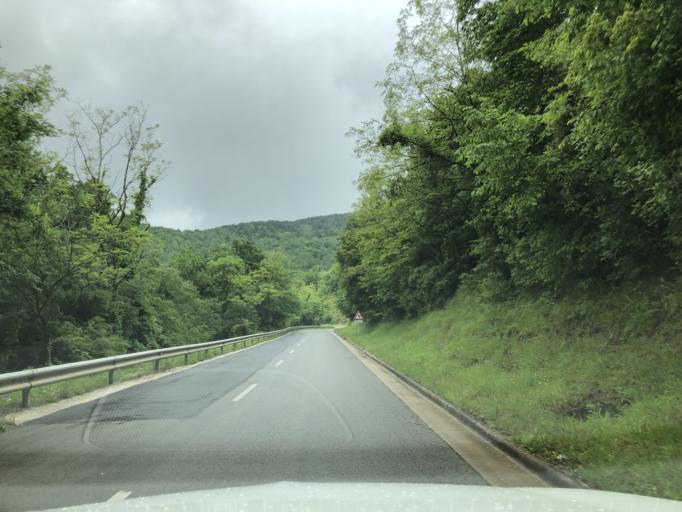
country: SI
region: Koper-Capodistria
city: Prade
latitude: 45.5049
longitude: 13.7734
